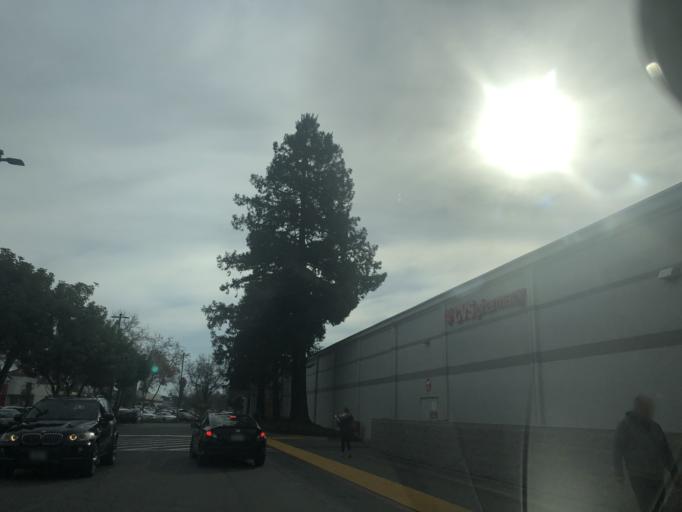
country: US
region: California
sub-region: Contra Costa County
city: Pacheco
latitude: 37.9772
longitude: -122.0666
